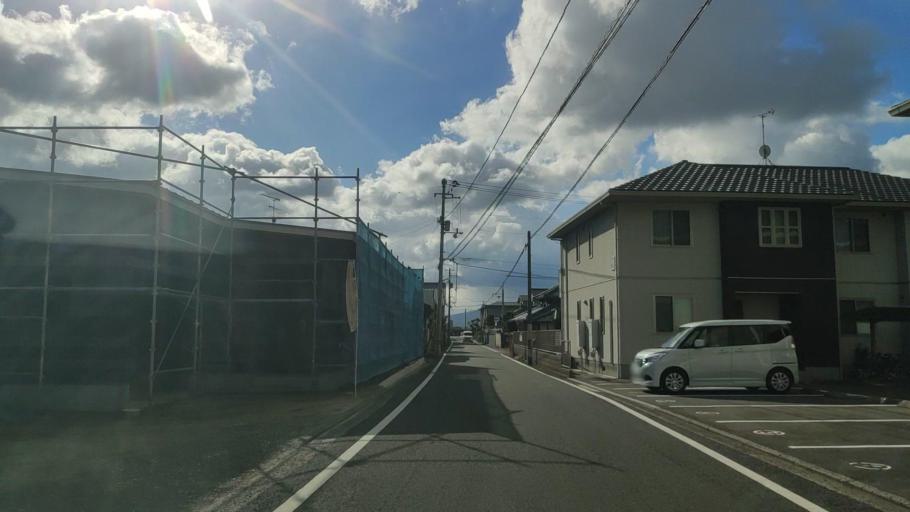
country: JP
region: Ehime
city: Masaki-cho
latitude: 33.8257
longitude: 132.7085
